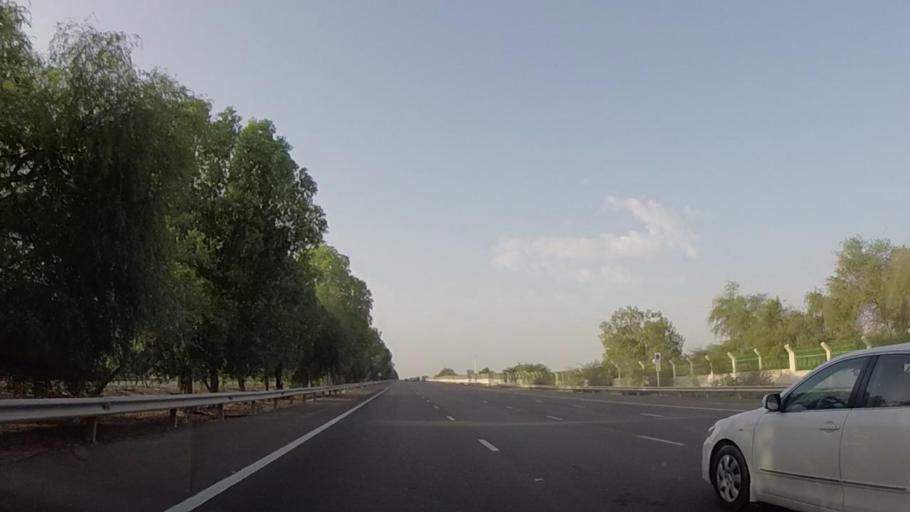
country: AE
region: Dubai
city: Dubai
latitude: 24.7618
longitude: 54.8432
